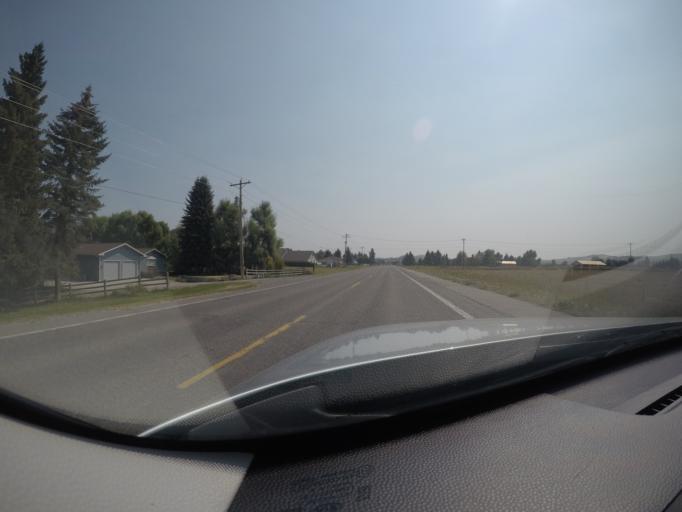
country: US
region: Montana
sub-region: Lake County
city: Polson
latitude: 47.7194
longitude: -114.1886
